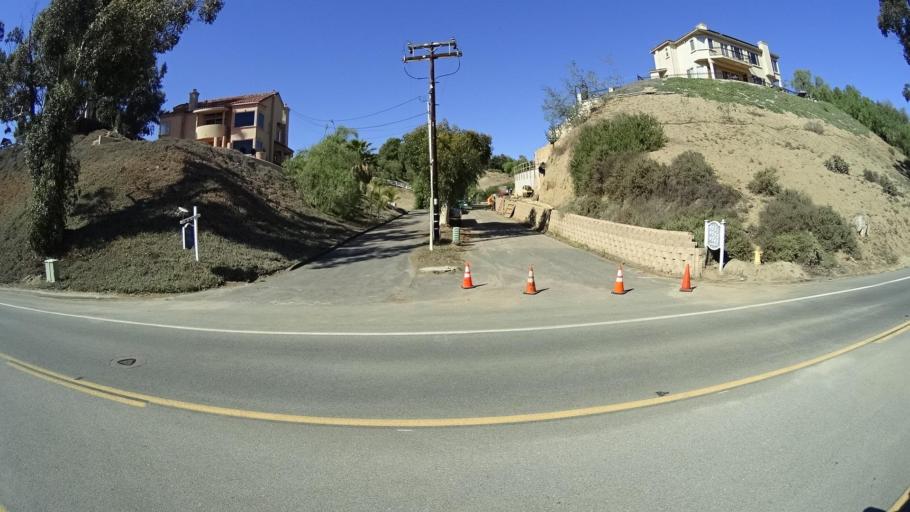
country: US
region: California
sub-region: San Diego County
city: Bonita
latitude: 32.6653
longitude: -117.0390
